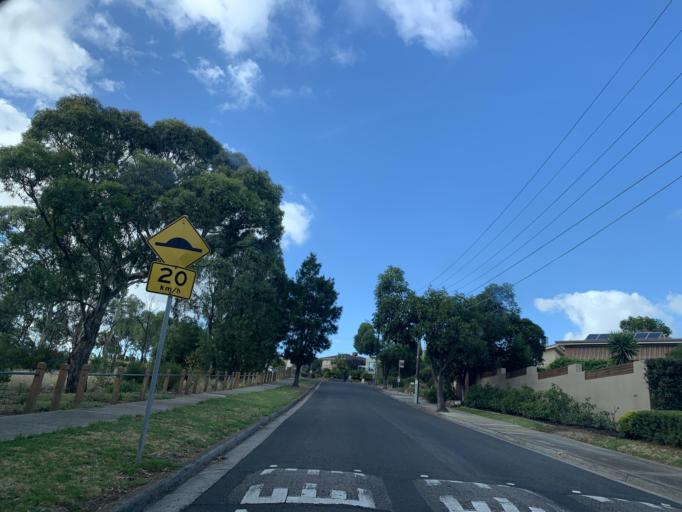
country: AU
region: Victoria
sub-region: Moreland
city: Gowanbrae
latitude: -37.7157
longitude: 144.8978
